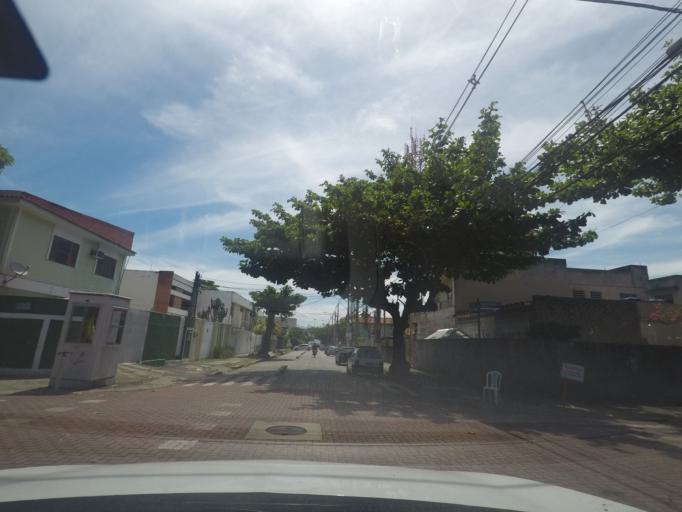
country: BR
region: Rio de Janeiro
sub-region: Niteroi
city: Niteroi
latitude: -22.9159
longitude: -43.0918
